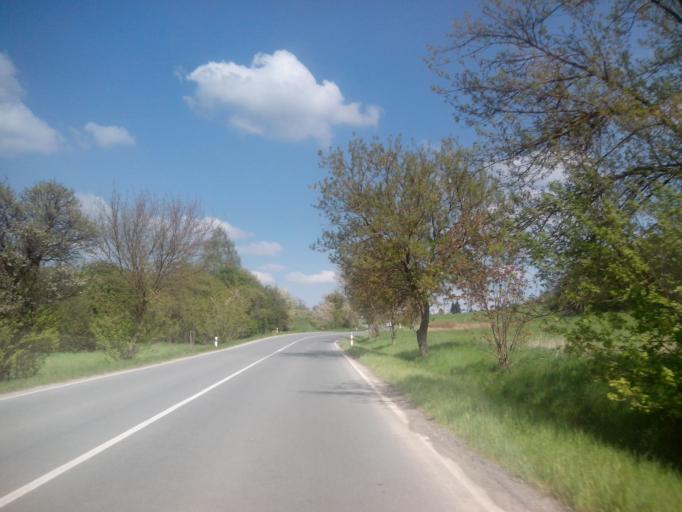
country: CZ
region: Central Bohemia
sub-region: Okres Beroun
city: Lodenice
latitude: 49.9799
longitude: 14.1175
